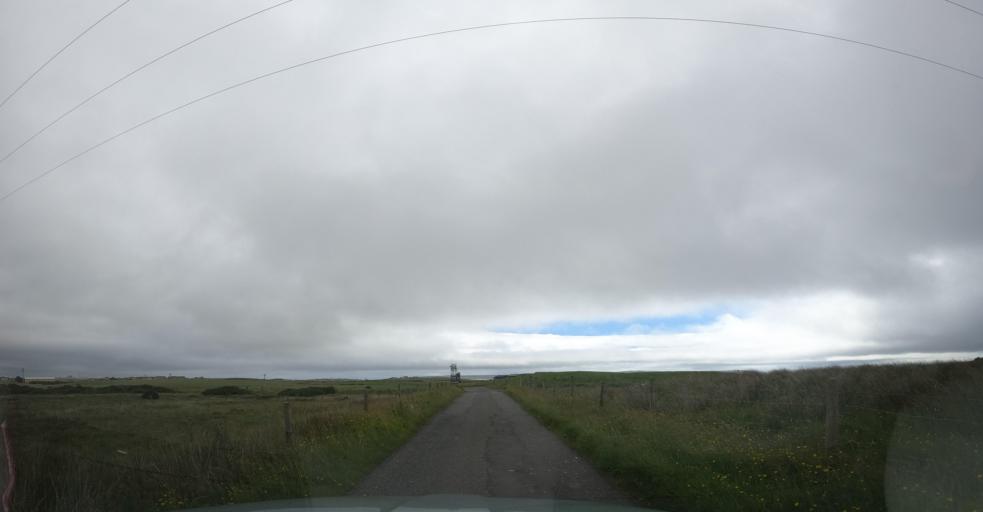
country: GB
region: Scotland
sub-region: Eilean Siar
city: Stornoway
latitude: 58.1924
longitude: -6.3485
